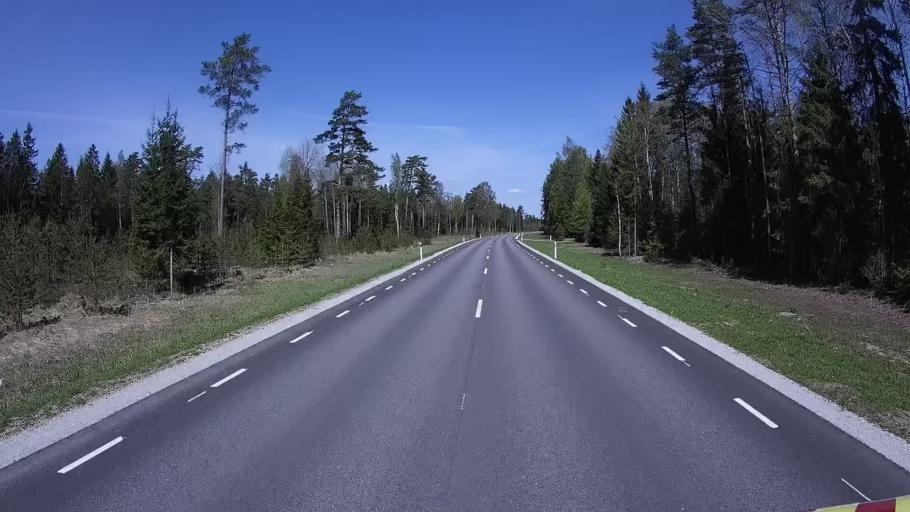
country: EE
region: Harju
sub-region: Nissi vald
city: Turba
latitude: 59.1392
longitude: 24.0755
